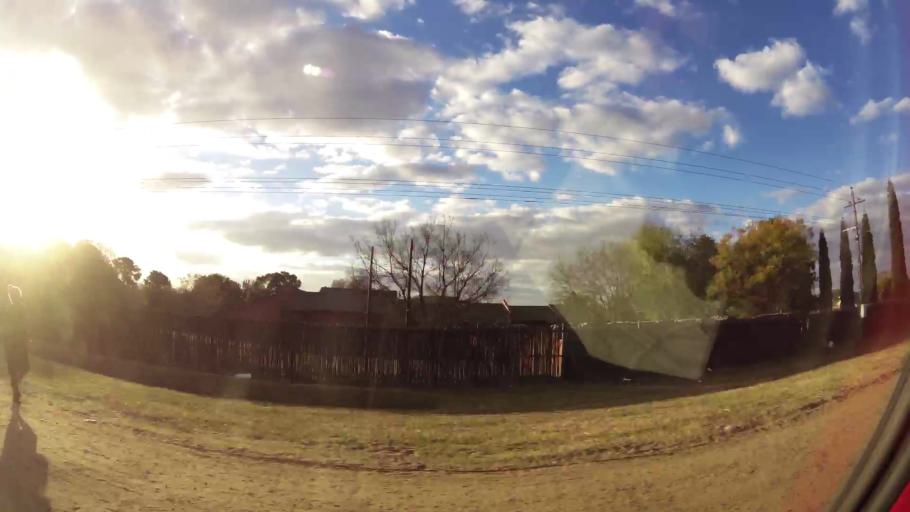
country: ZA
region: Gauteng
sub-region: City of Johannesburg Metropolitan Municipality
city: Midrand
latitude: -25.9568
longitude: 28.1699
